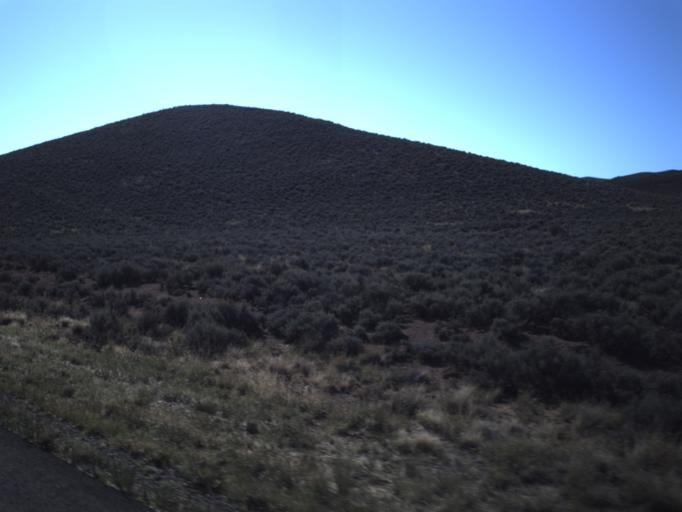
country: US
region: Utah
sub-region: Washington County
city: Enterprise
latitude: 37.7429
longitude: -113.7494
